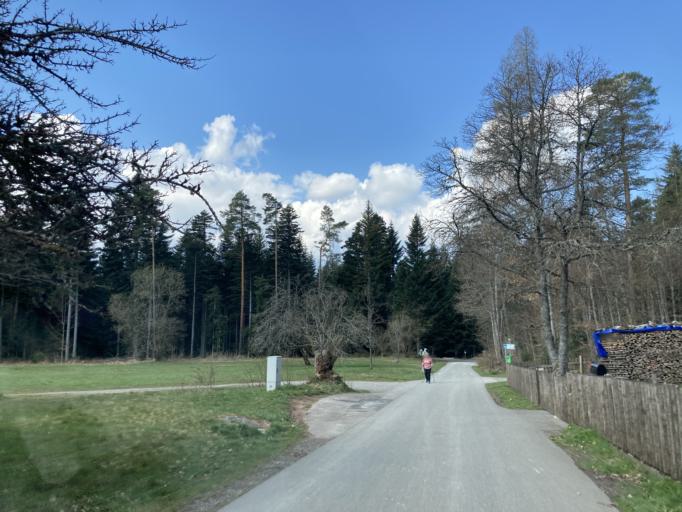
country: DE
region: Baden-Wuerttemberg
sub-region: Karlsruhe Region
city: Schomberg
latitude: 48.7840
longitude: 8.6294
